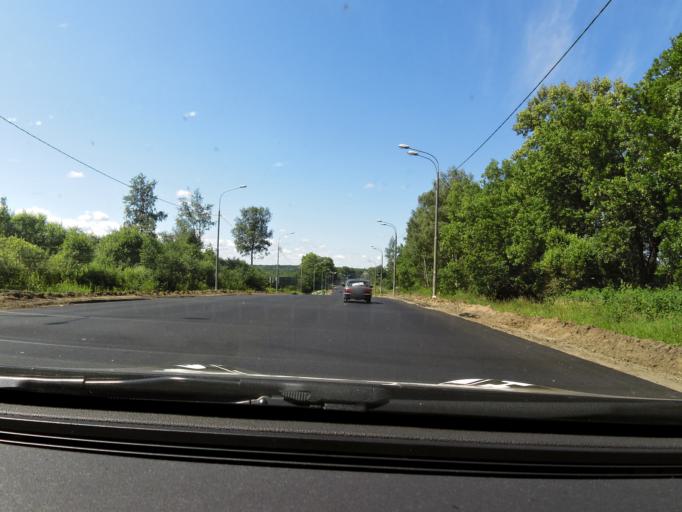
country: RU
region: Novgorod
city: Valday
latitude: 57.9531
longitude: 33.2760
